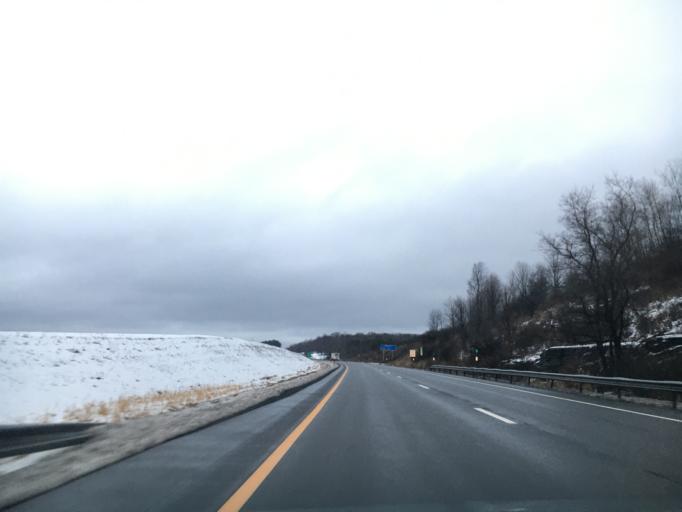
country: US
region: New York
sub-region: Cortland County
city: Cortland
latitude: 42.5945
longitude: -76.1371
